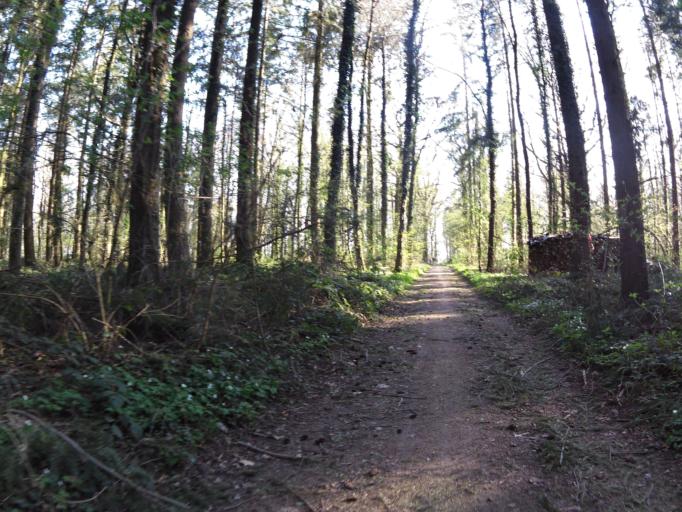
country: DE
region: Bavaria
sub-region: Regierungsbezirk Unterfranken
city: Kurnach
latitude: 49.8266
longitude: 10.0605
